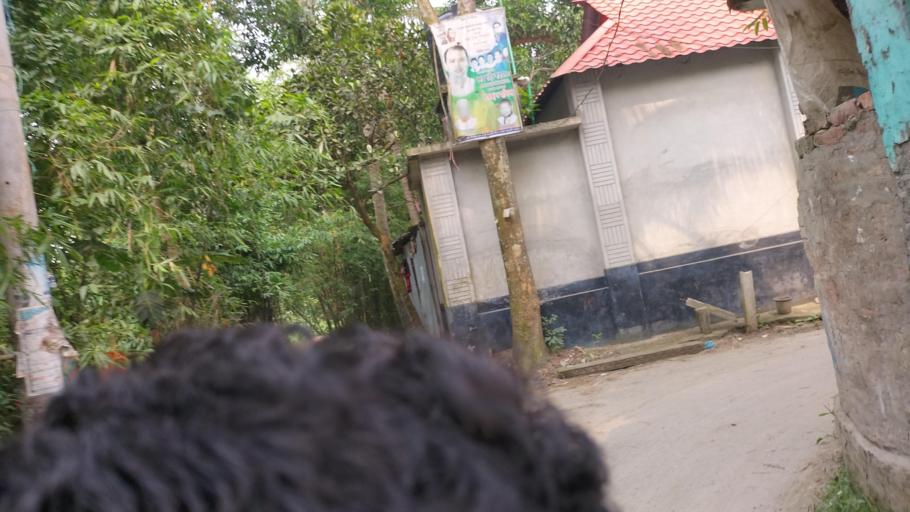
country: BD
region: Dhaka
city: Azimpur
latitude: 23.6936
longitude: 90.2999
